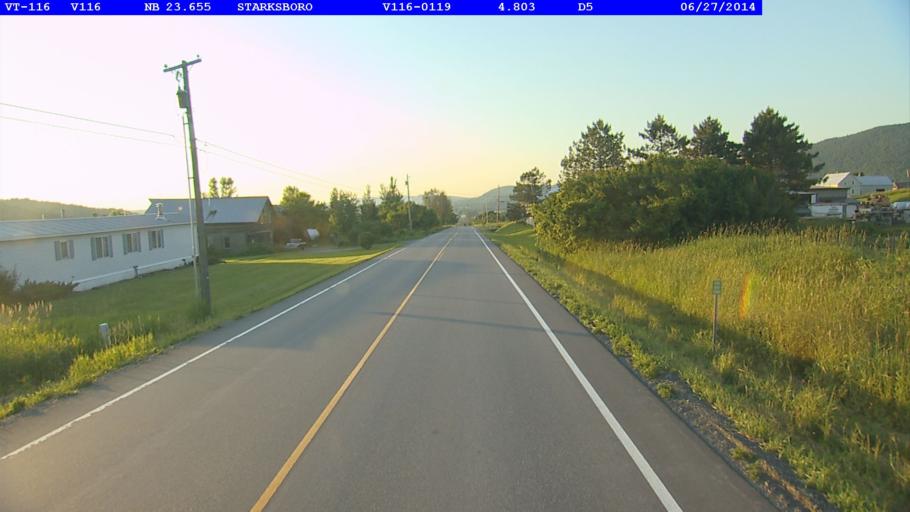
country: US
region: Vermont
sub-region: Chittenden County
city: Hinesburg
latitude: 44.2534
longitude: -73.0630
